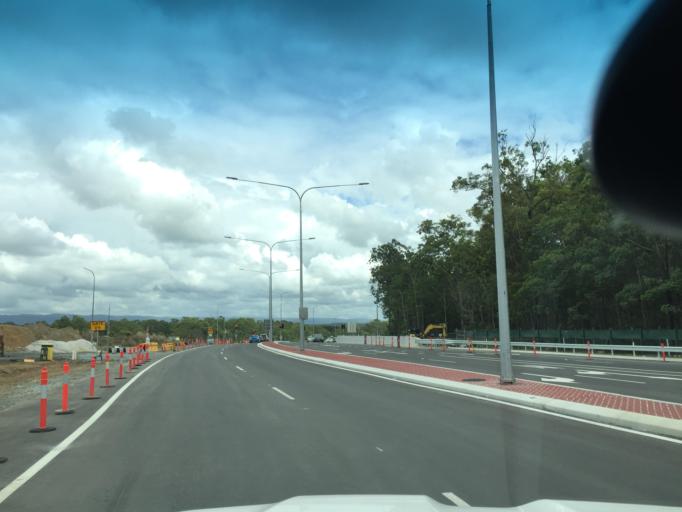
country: AU
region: Queensland
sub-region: Moreton Bay
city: Burpengary
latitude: -27.1777
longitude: 152.9863
